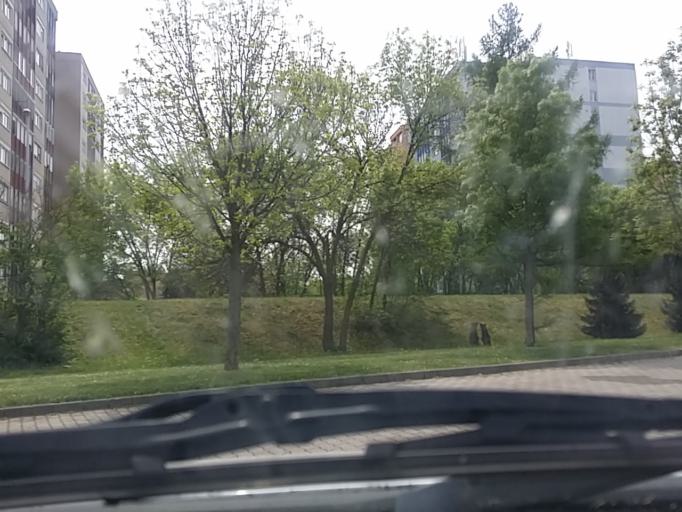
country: HU
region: Zala
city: Nagykanizsa
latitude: 46.4632
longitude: 17.0136
